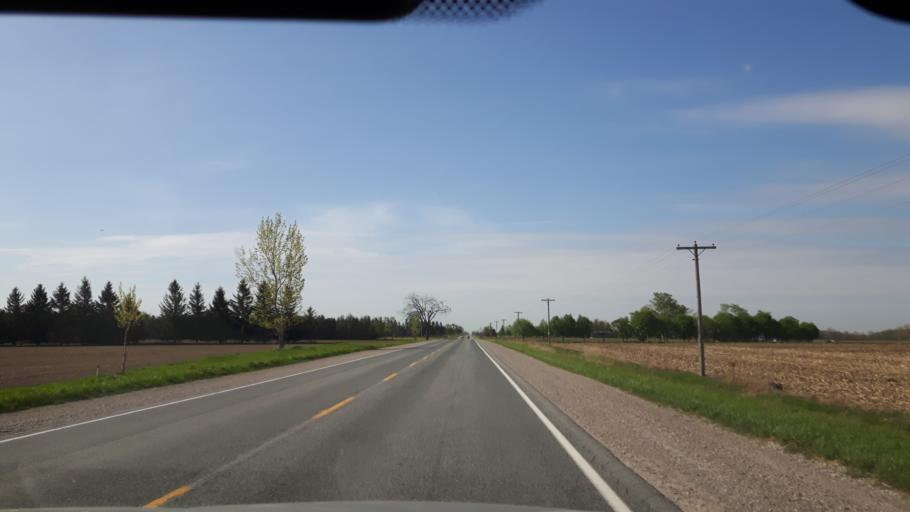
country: CA
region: Ontario
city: Bluewater
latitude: 43.5051
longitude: -81.5131
